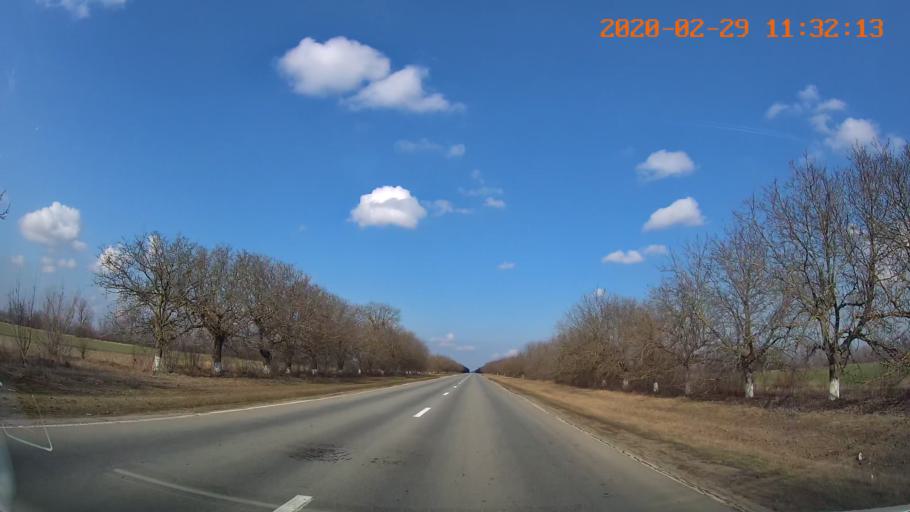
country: MD
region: Rezina
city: Saharna
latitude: 47.5349
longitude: 29.0967
